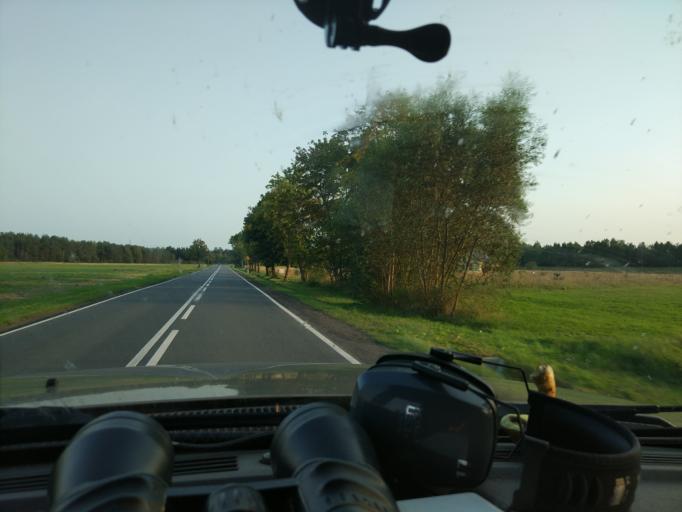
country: PL
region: Masovian Voivodeship
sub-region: Powiat przasnyski
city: Chorzele
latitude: 53.2776
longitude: 20.8991
